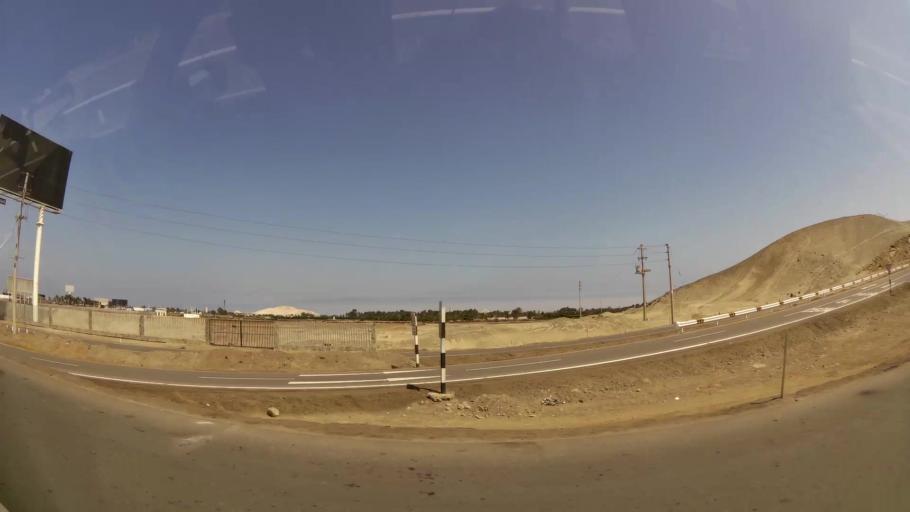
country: PE
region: Lima
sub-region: Provincia de Canete
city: Asia
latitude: -12.7569
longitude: -76.6039
